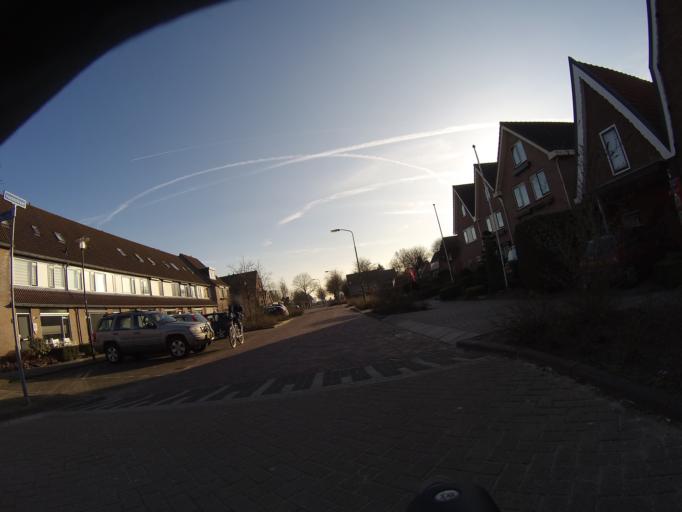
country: NL
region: Utrecht
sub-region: Gemeente Bunschoten
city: Bunschoten
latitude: 52.2325
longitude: 5.3716
